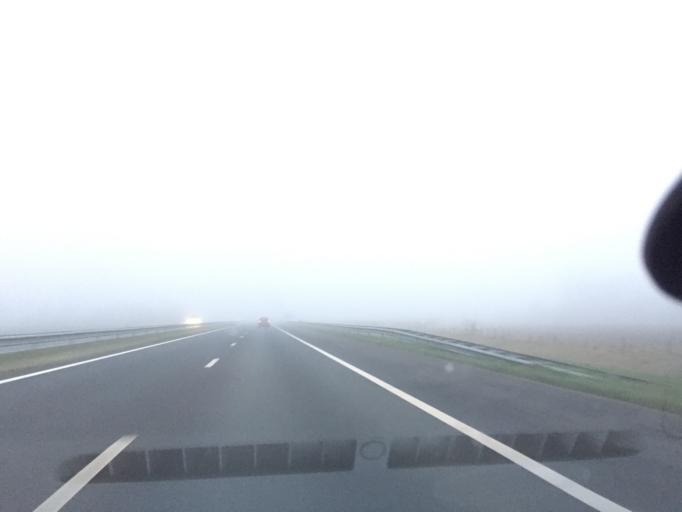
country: NL
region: Gelderland
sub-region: Gemeente Doetinchem
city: Doetinchem
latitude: 51.9446
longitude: 6.2356
